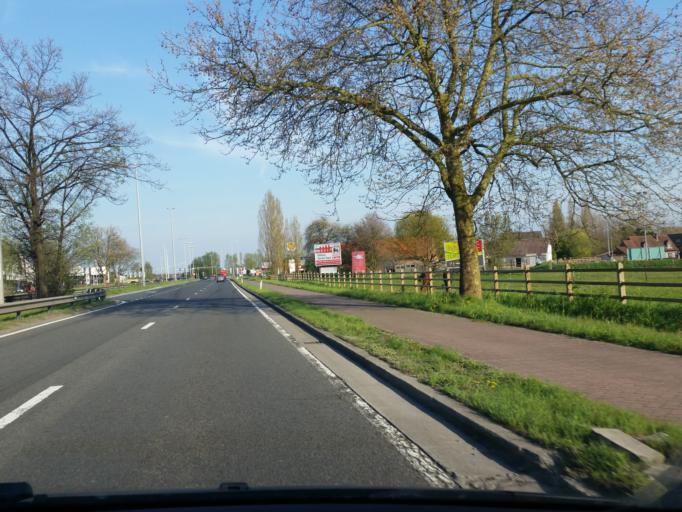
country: BE
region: Flanders
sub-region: Provincie Oost-Vlaanderen
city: Temse
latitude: 51.1359
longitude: 4.1832
